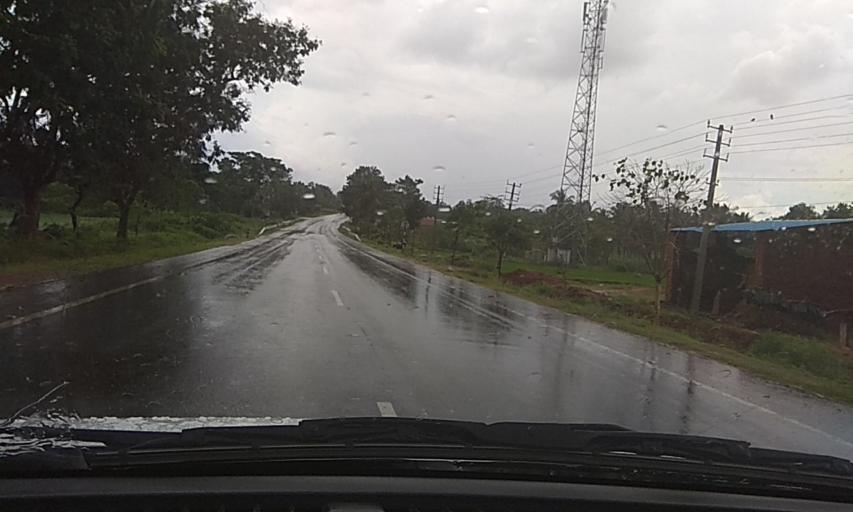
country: IN
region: Karnataka
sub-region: Tumkur
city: Kunigal
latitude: 12.9570
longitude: 77.0280
